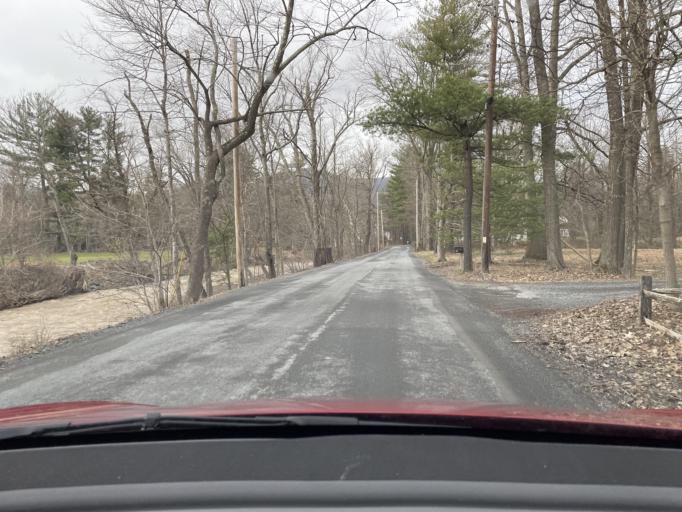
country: US
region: New York
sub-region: Ulster County
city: Woodstock
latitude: 42.0349
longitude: -74.1054
